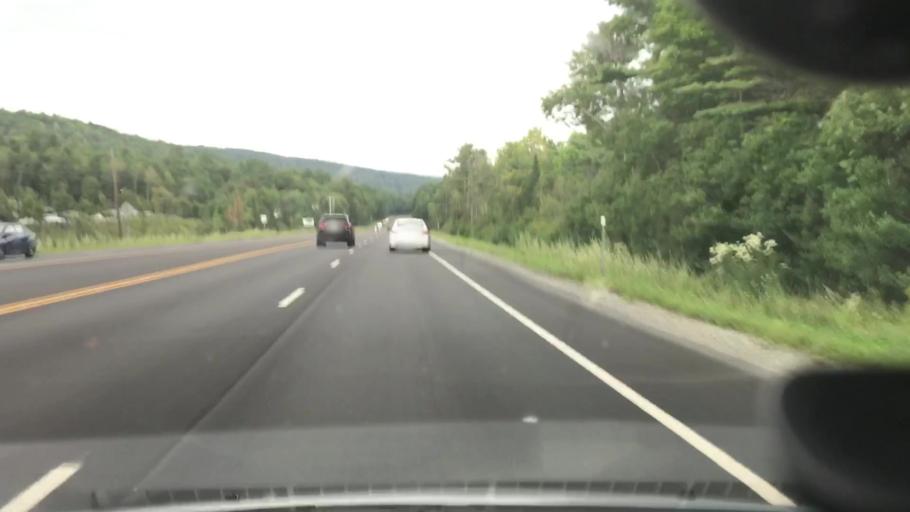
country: US
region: New Hampshire
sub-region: Grafton County
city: Lebanon
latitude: 43.6725
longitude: -72.2589
